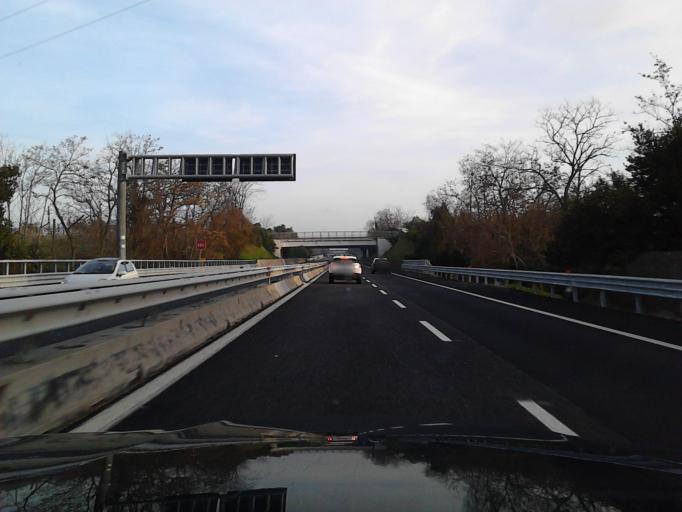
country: IT
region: Abruzzo
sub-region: Provincia di Chieti
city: Ortona
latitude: 42.3284
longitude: 14.3849
